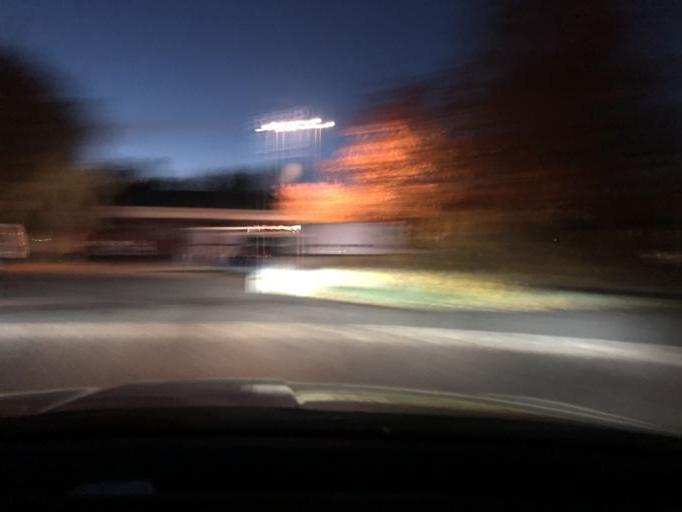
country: SE
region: Stockholm
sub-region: Botkyrka Kommun
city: Alby
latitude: 59.2345
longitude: 17.8472
